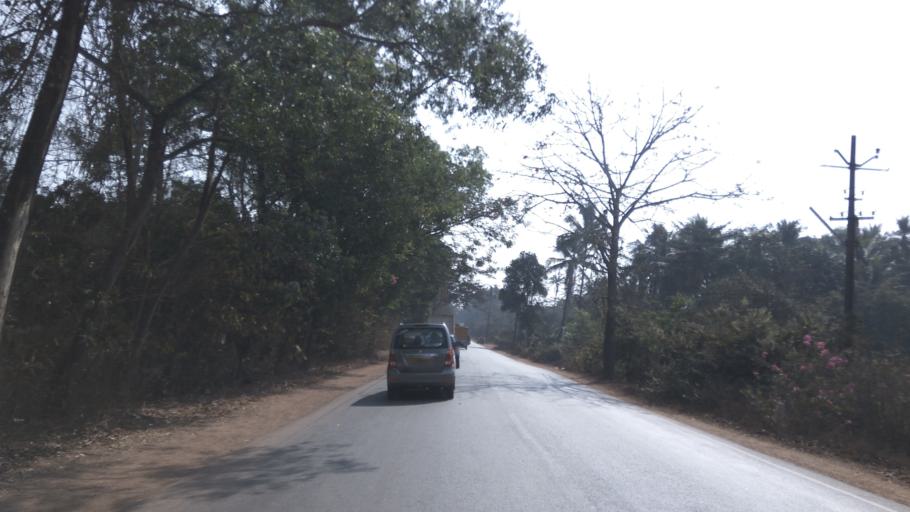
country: IN
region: Goa
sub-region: North Goa
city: Curti
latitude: 15.4178
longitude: 74.0632
